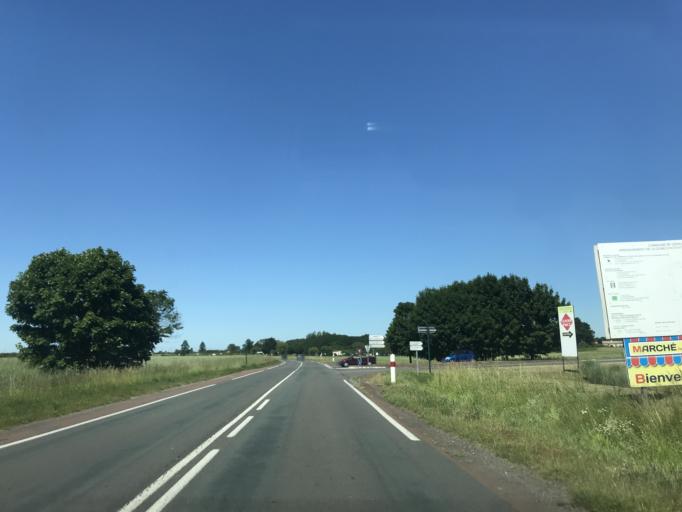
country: FR
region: Poitou-Charentes
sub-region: Departement de la Charente-Maritime
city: Gemozac
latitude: 45.5768
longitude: -0.6810
